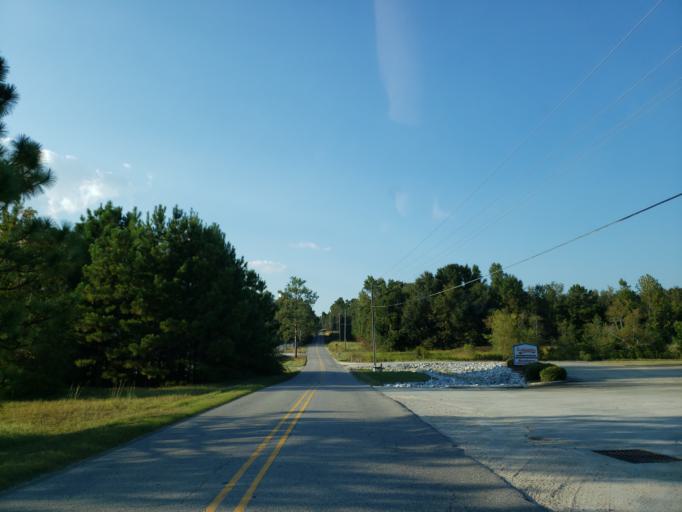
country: US
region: Mississippi
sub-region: Lamar County
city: West Hattiesburg
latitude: 31.3197
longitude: -89.4442
